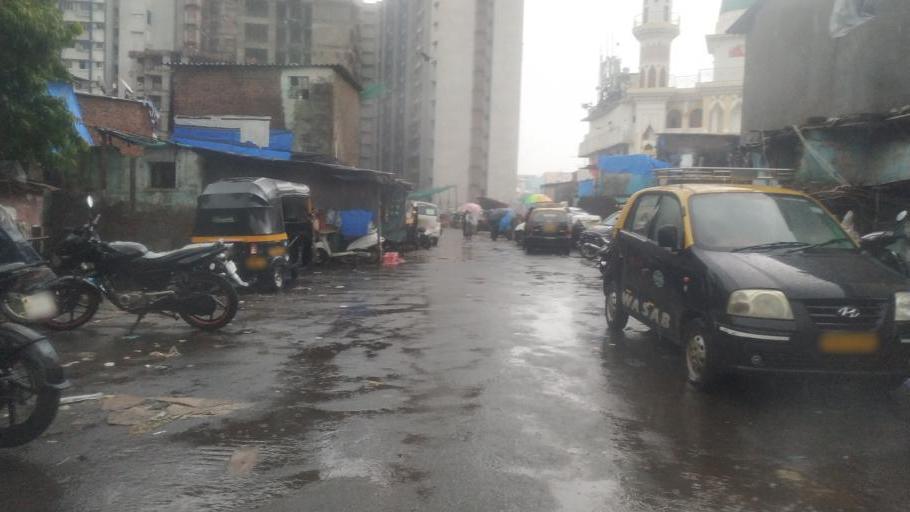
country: IN
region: Maharashtra
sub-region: Mumbai Suburban
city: Mumbai
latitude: 19.0639
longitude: 72.8557
